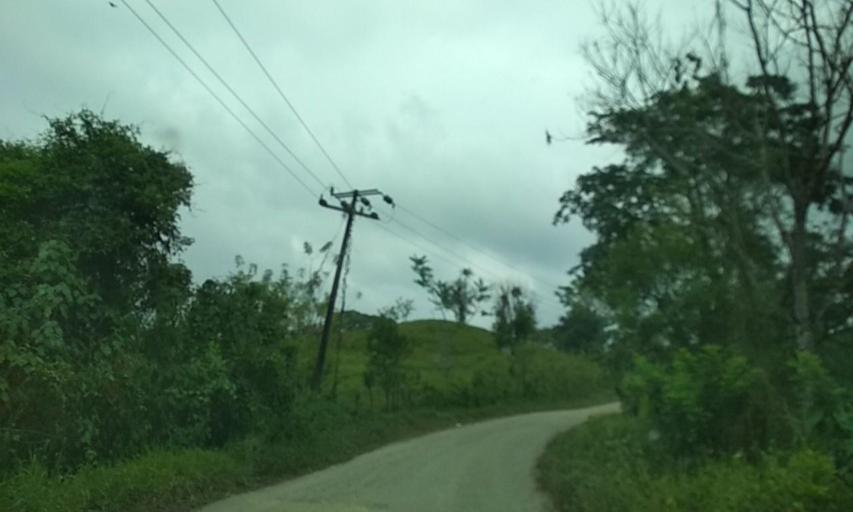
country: MX
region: Veracruz
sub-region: Uxpanapa
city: Poblado 10
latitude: 17.4913
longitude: -94.1308
